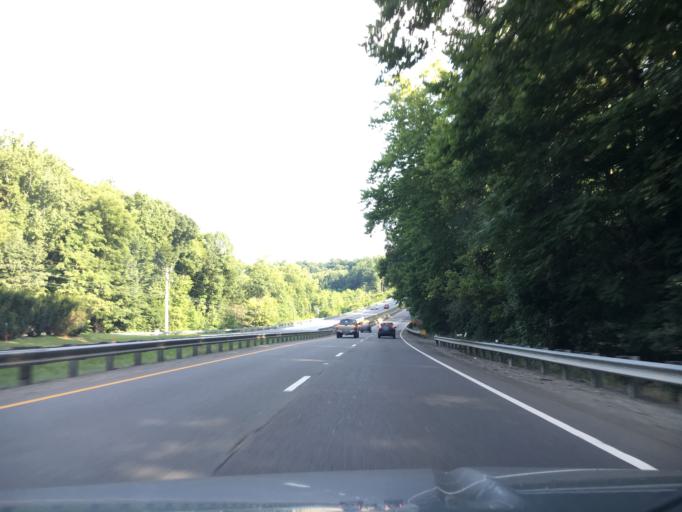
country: US
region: Virginia
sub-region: Franklin County
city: Rocky Mount
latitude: 37.0557
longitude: -79.8828
